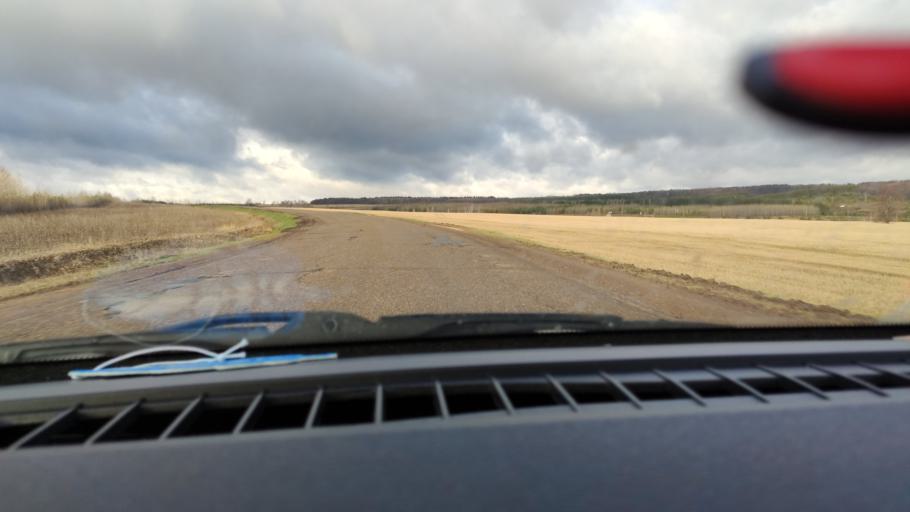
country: RU
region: Tatarstan
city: Russkiy Aktash
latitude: 55.0367
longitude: 52.0259
